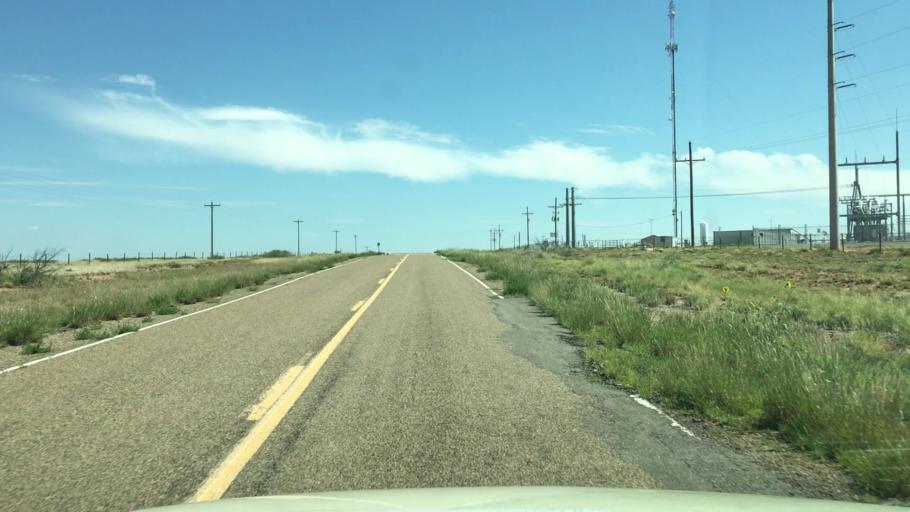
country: US
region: New Mexico
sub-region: Chaves County
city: Roswell
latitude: 33.9627
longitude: -104.5829
